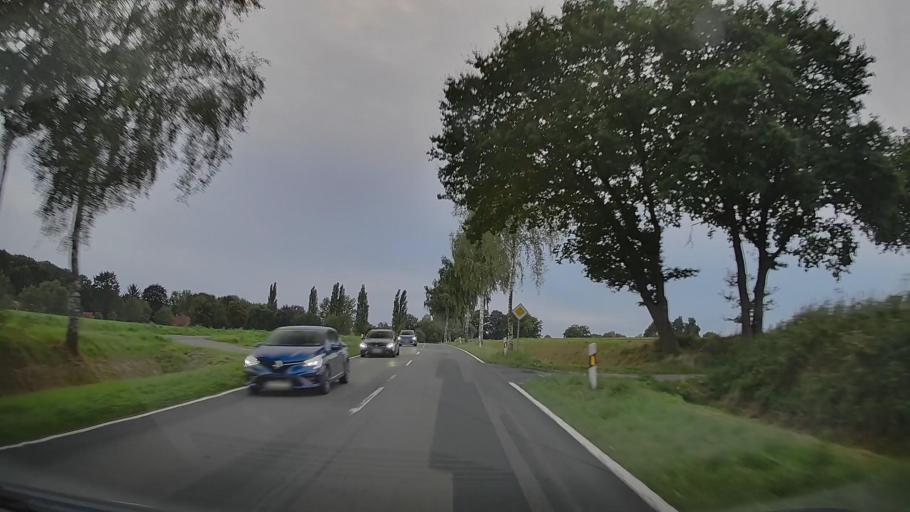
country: DE
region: Lower Saxony
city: Sustedt
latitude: 52.9048
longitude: 8.8873
